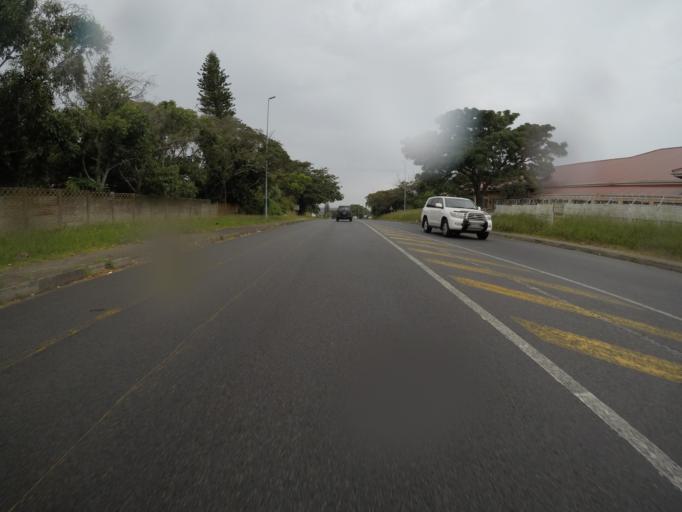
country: ZA
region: Eastern Cape
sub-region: Buffalo City Metropolitan Municipality
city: East London
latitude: -32.9844
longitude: 27.8603
